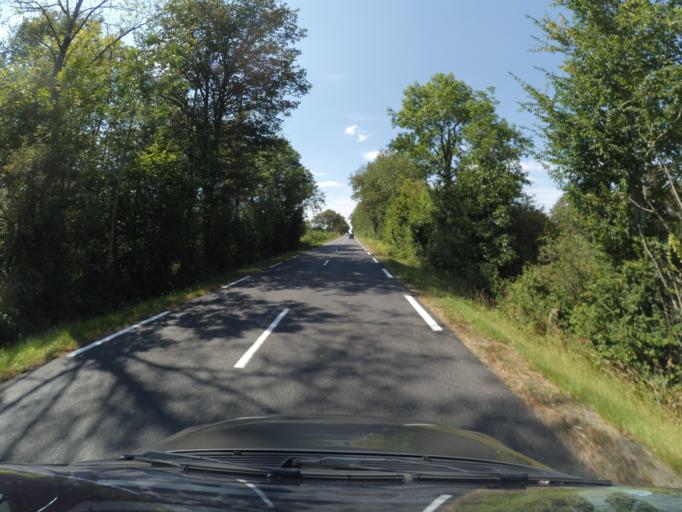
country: FR
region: Limousin
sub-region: Departement de la Haute-Vienne
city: Bussiere-Poitevine
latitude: 46.2311
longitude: 0.9716
